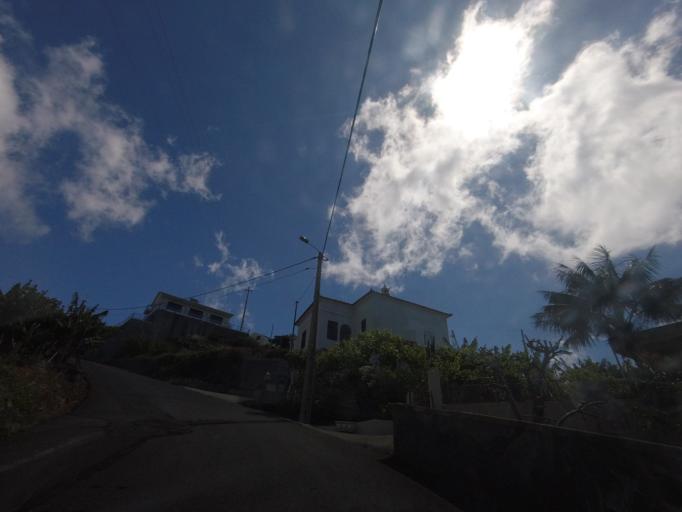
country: PT
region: Madeira
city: Ponta do Sol
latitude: 32.6821
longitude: -17.0825
